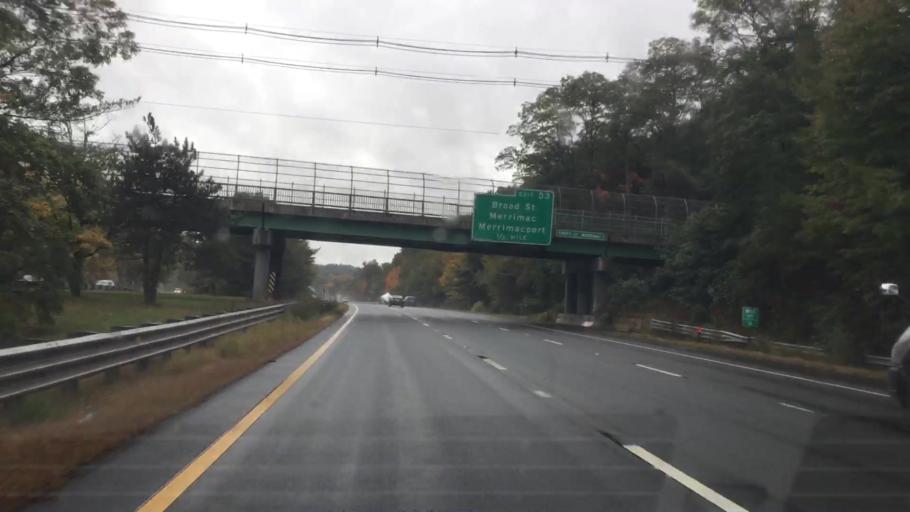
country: US
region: Massachusetts
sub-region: Essex County
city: Merrimac
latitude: 42.8339
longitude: -70.9781
